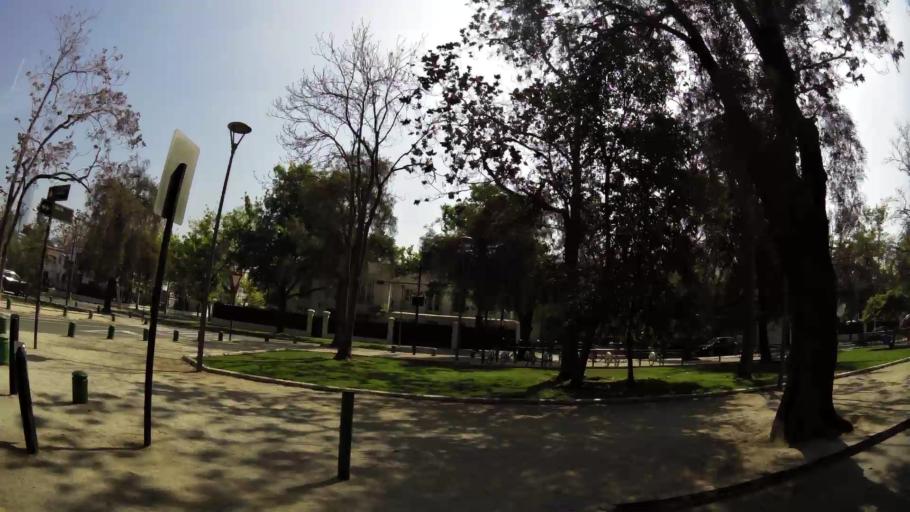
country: CL
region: Santiago Metropolitan
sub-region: Provincia de Santiago
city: Villa Presidente Frei, Nunoa, Santiago, Chile
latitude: -33.4211
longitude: -70.5922
